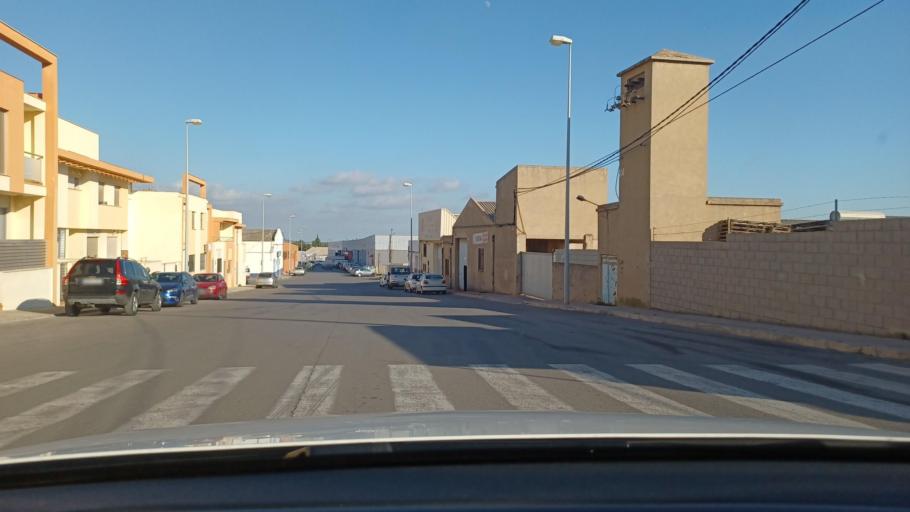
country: ES
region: Valencia
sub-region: Provincia de Castello
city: Onda
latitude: 39.9618
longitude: -0.2446
